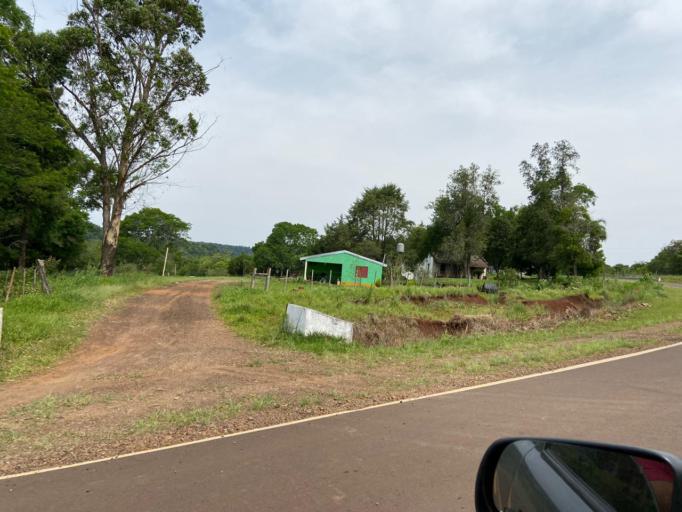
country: AR
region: Misiones
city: Arroyo del Medio
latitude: -27.6793
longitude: -55.3993
